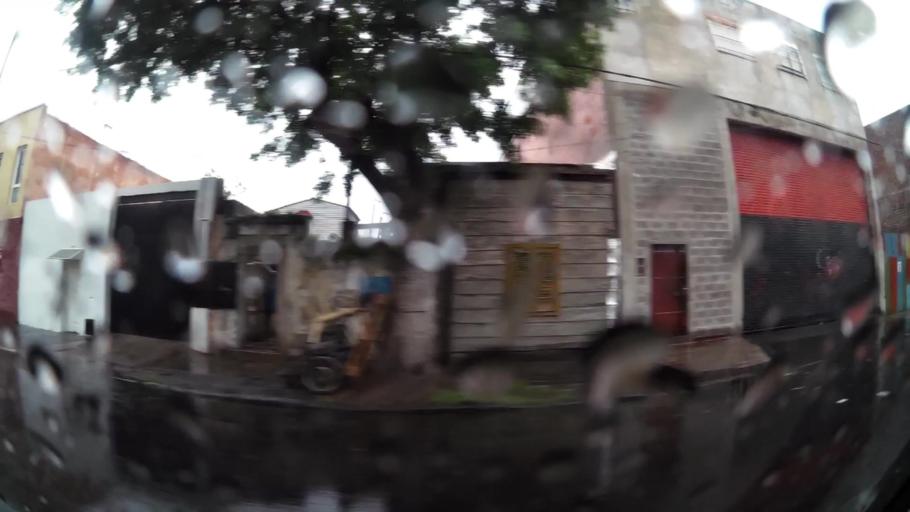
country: AR
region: Buenos Aires
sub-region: Partido de Avellaneda
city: Avellaneda
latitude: -34.6432
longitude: -58.3639
